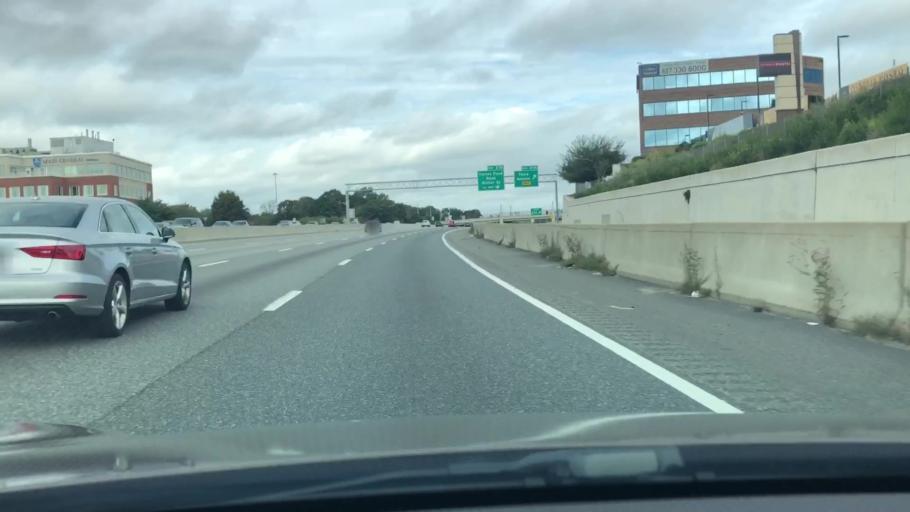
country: US
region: Massachusetts
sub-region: Middlesex County
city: Waltham
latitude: 42.3936
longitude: -71.2622
